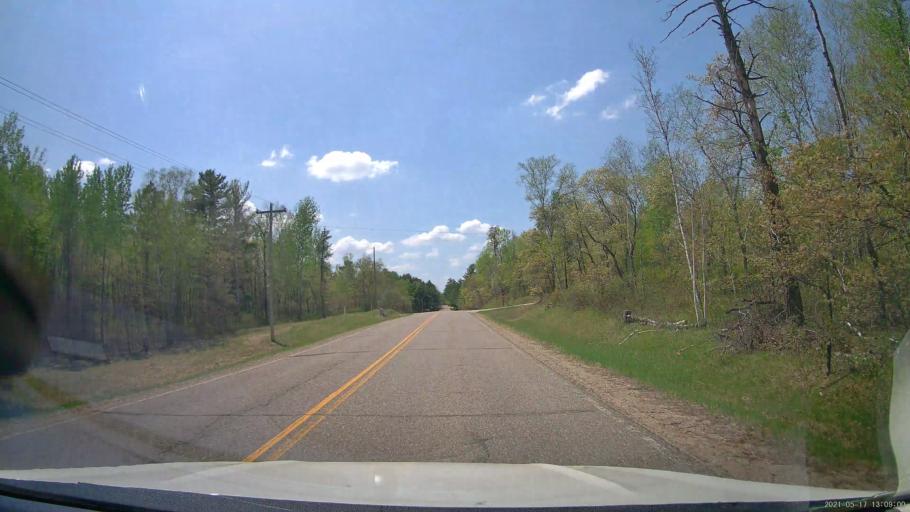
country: US
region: Minnesota
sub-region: Hubbard County
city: Park Rapids
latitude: 47.0314
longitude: -94.9233
